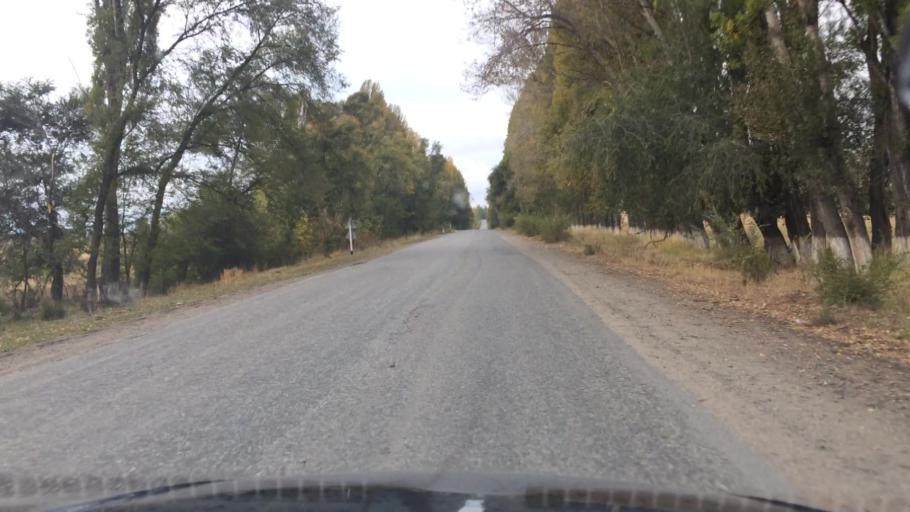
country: KG
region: Ysyk-Koel
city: Pokrovka
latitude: 42.7396
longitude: 77.8994
